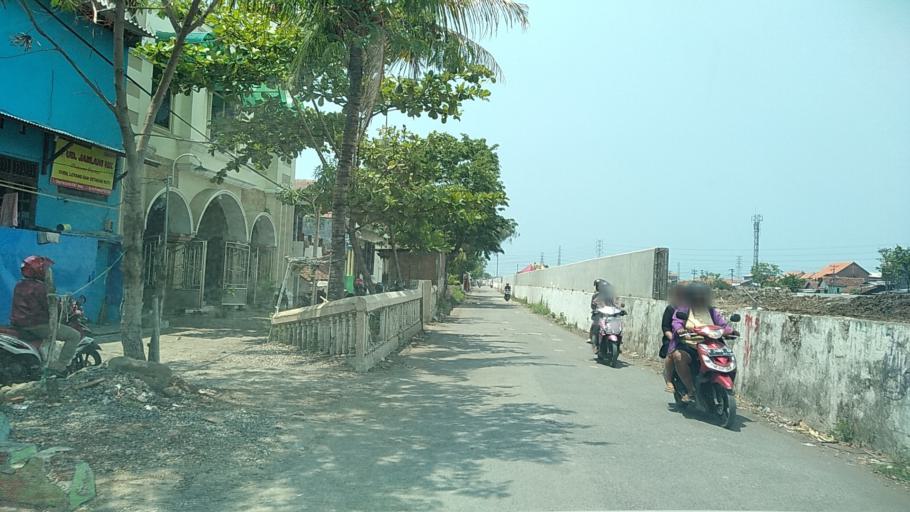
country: ID
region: Central Java
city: Semarang
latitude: -6.9590
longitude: 110.4417
